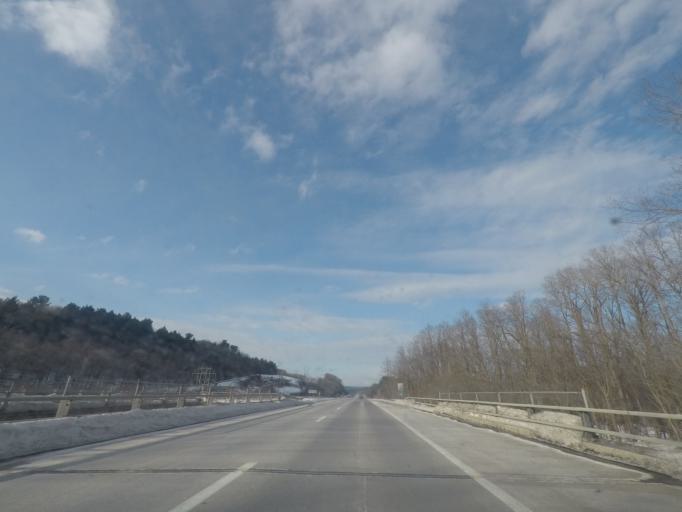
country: US
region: New York
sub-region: Schenectady County
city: Scotia
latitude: 42.8209
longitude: -73.9892
